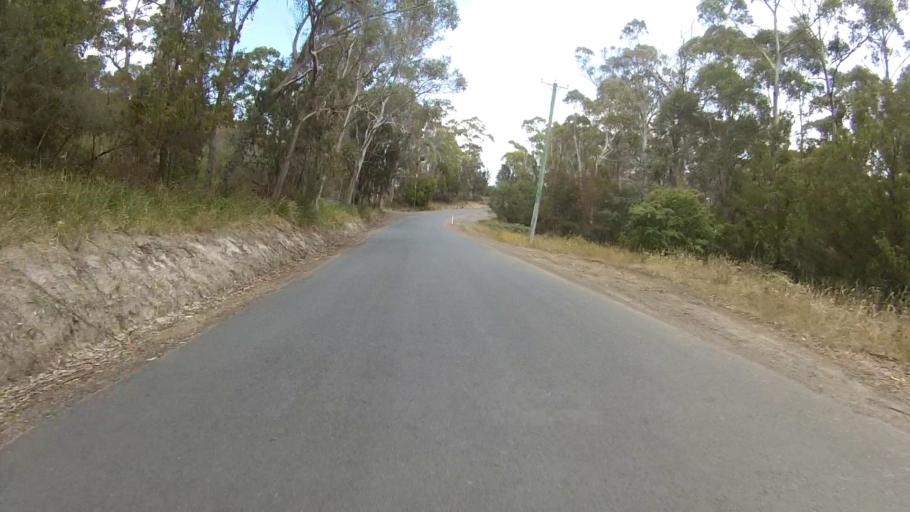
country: AU
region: Tasmania
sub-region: Kingborough
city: Blackmans Bay
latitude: -43.0245
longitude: 147.3135
